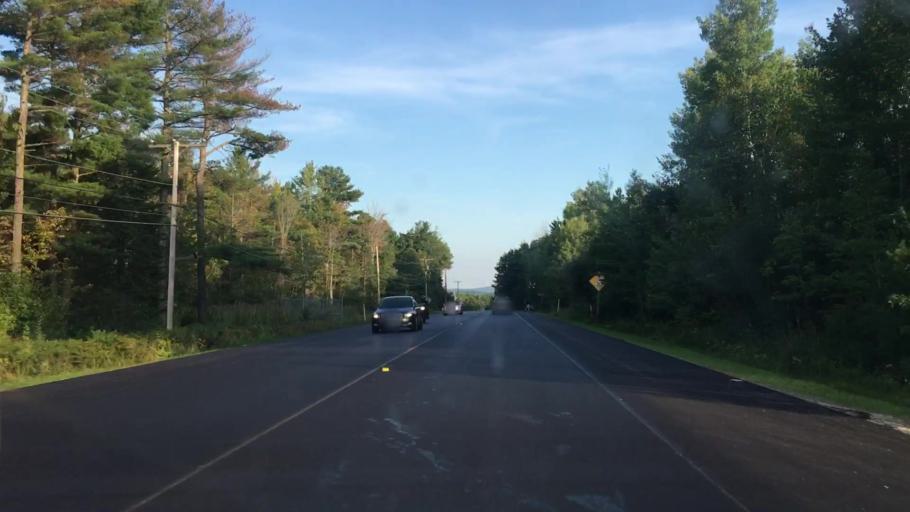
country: US
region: Maine
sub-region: Penobscot County
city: Hampden
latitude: 44.7572
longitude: -68.8435
